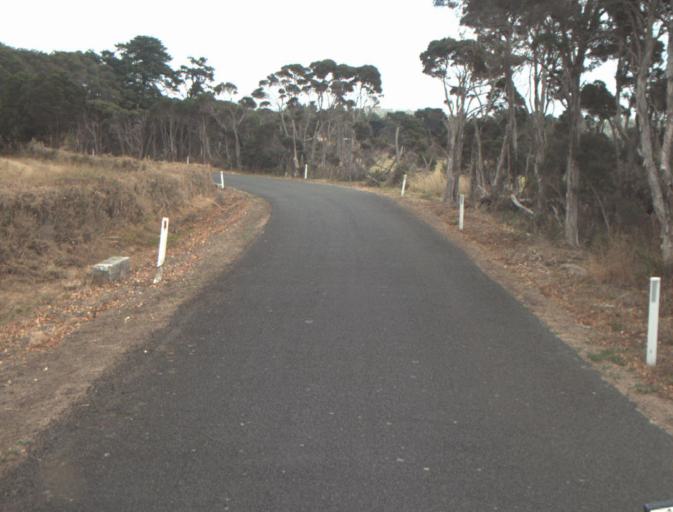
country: AU
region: Tasmania
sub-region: Launceston
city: Mayfield
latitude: -41.2898
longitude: 146.9908
